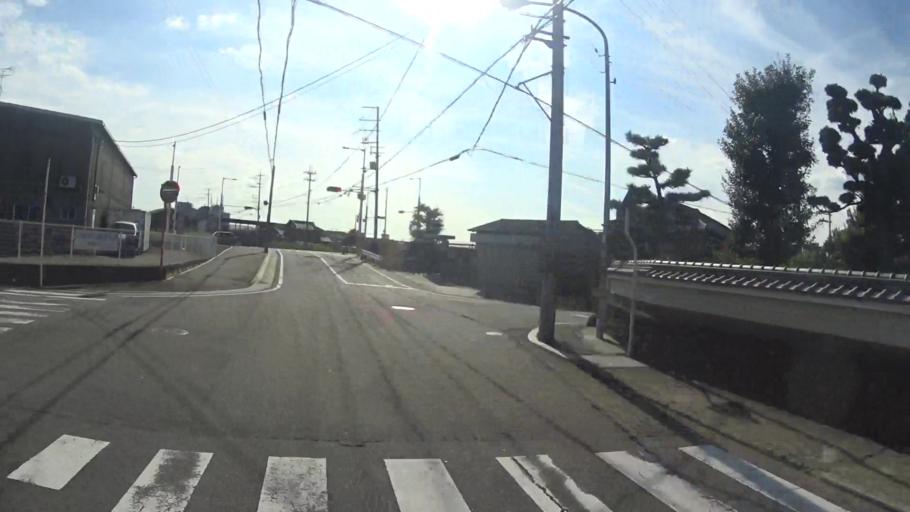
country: JP
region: Kyoto
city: Yawata
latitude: 34.8680
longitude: 135.7307
